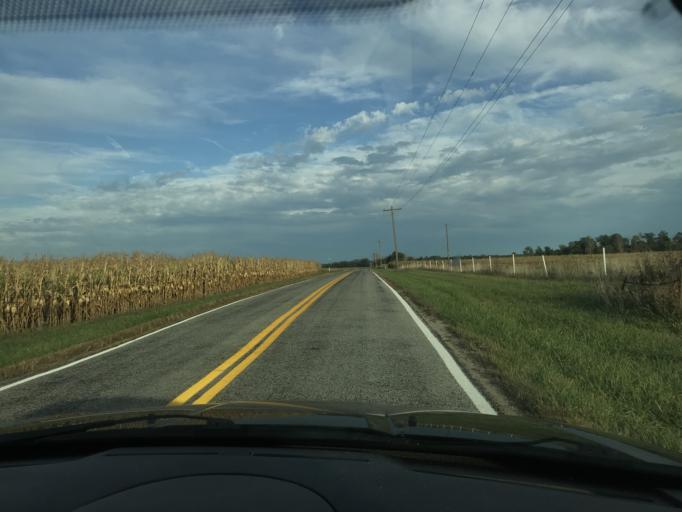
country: US
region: Ohio
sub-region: Logan County
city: West Liberty
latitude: 40.2174
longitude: -83.8092
